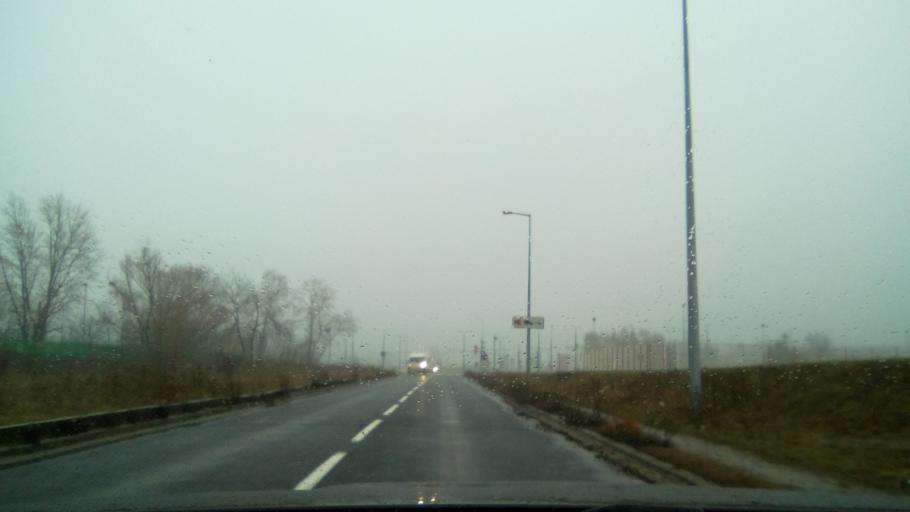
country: PL
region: Greater Poland Voivodeship
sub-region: Poznan
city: Poznan
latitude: 52.3837
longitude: 16.9988
